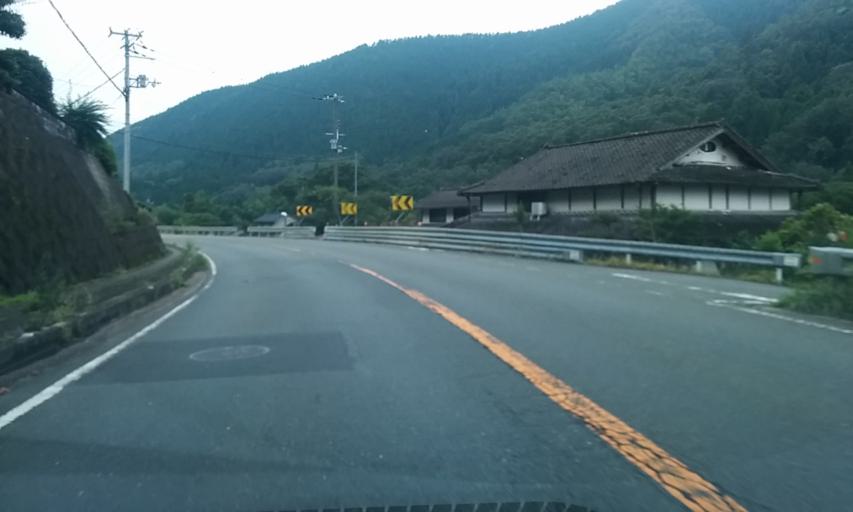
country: JP
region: Kyoto
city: Ayabe
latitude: 35.2359
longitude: 135.4130
